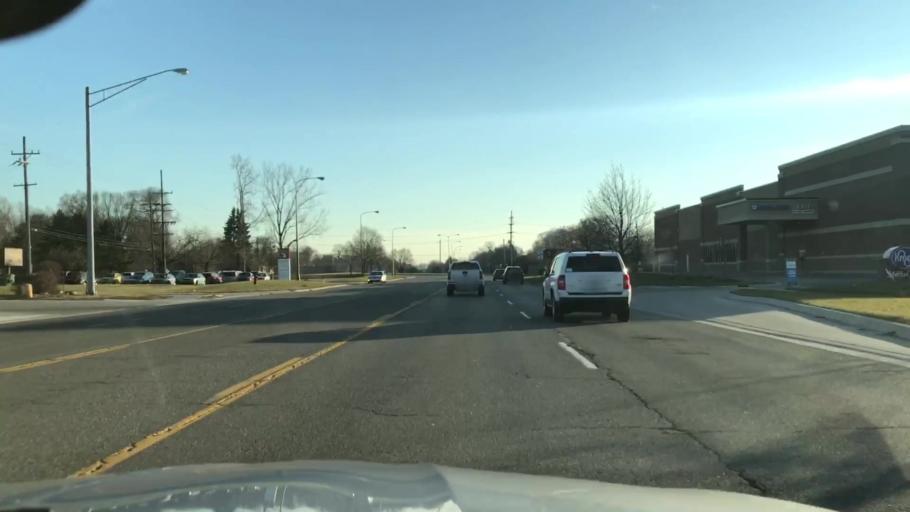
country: US
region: Michigan
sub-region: Oakland County
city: Madison Heights
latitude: 42.5024
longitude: -83.1180
